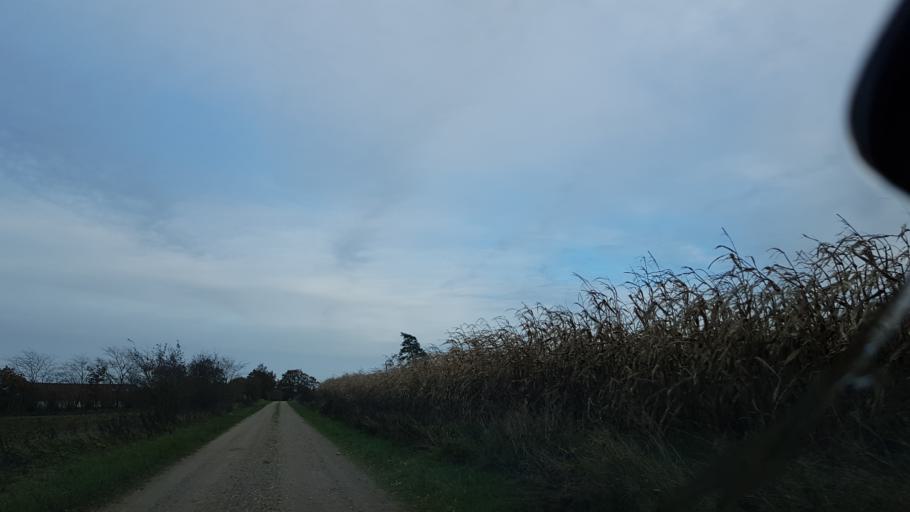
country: DK
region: South Denmark
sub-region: Haderslev Kommune
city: Vojens
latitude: 55.2924
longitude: 9.2205
